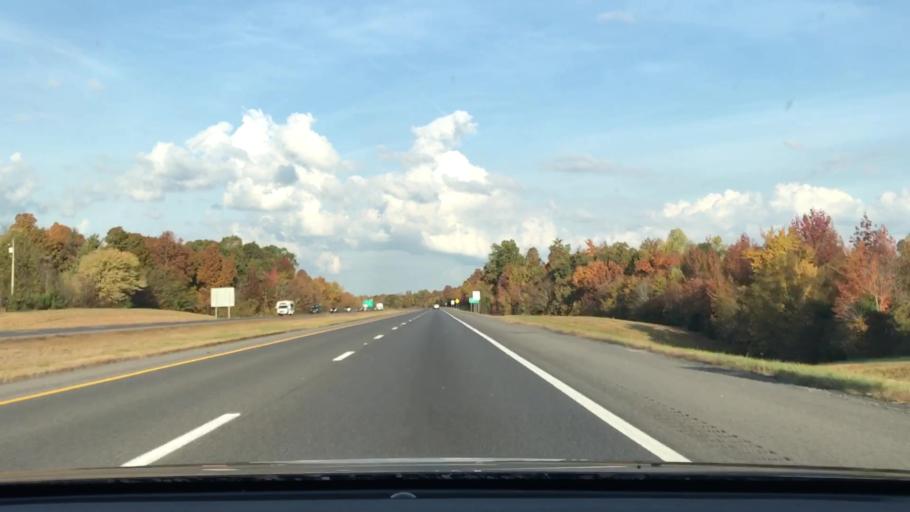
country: US
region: Kentucky
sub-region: Lyon County
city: Eddyville
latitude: 37.0611
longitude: -88.0398
